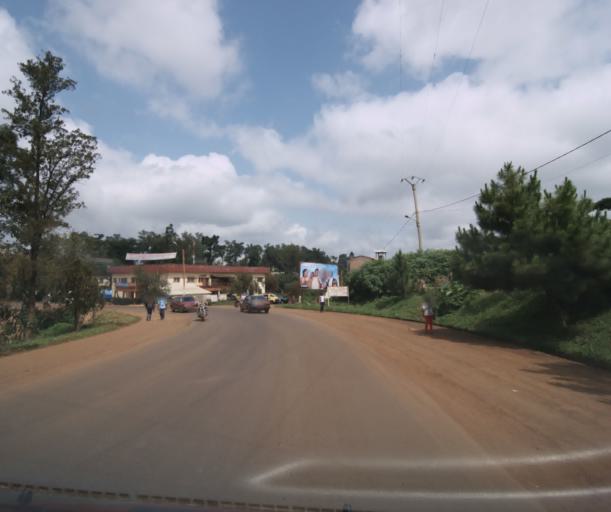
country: CM
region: West
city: Dschang
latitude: 5.4507
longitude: 10.0626
